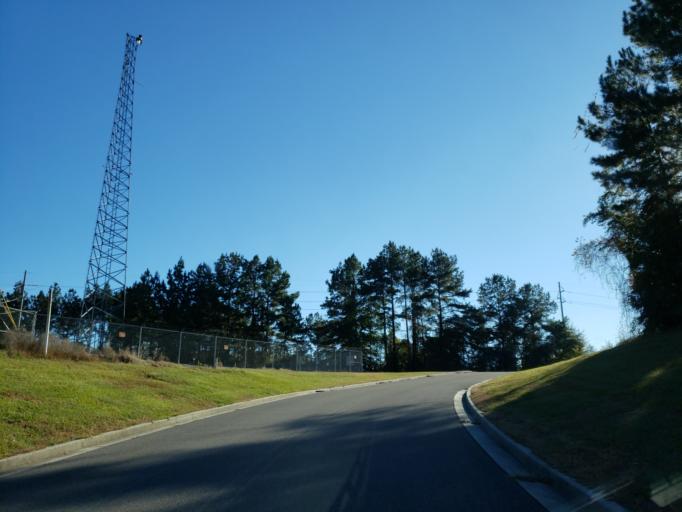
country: US
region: Mississippi
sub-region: Forrest County
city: Hattiesburg
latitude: 31.2530
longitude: -89.2758
